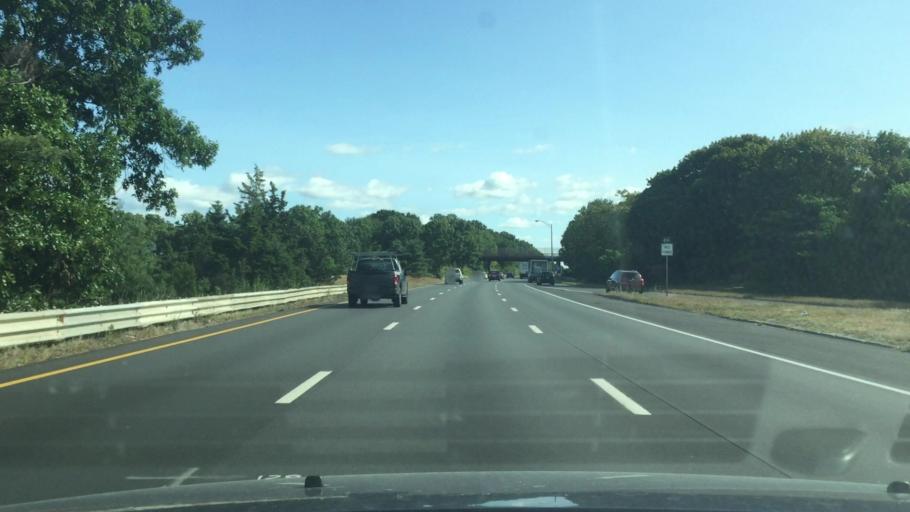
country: US
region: Massachusetts
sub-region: Essex County
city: Lawrence
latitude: 42.6655
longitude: -71.1922
